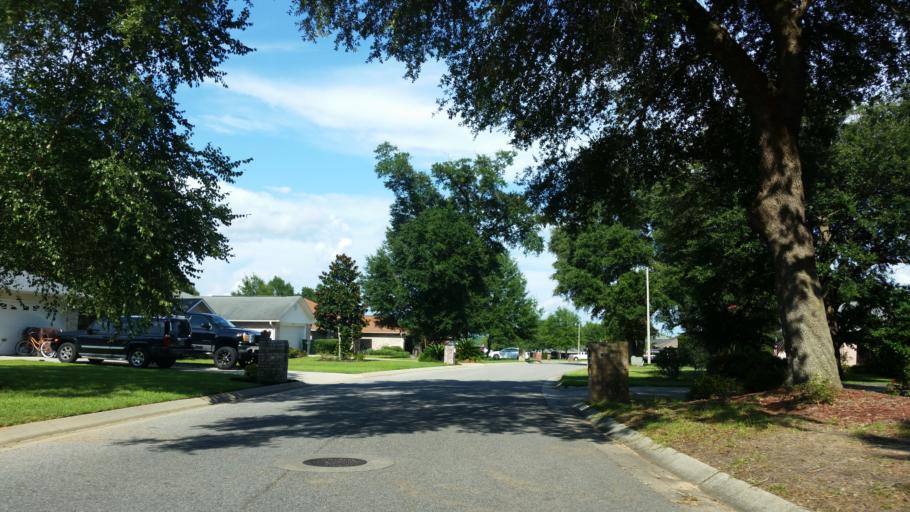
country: US
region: Florida
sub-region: Santa Rosa County
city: Pace
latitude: 30.6199
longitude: -87.1208
